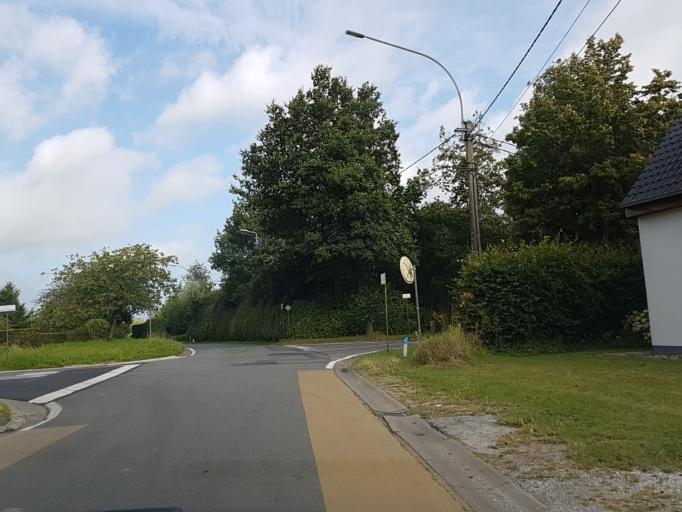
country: BE
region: Flanders
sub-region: Provincie Oost-Vlaanderen
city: Sint-Martens-Latem
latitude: 51.0556
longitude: 3.6462
